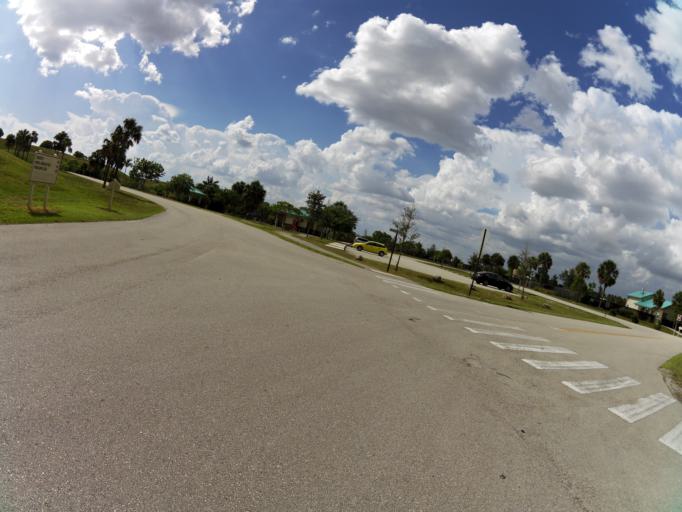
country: US
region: Florida
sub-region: Broward County
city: Southwest Ranches
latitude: 26.0680
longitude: -80.3398
